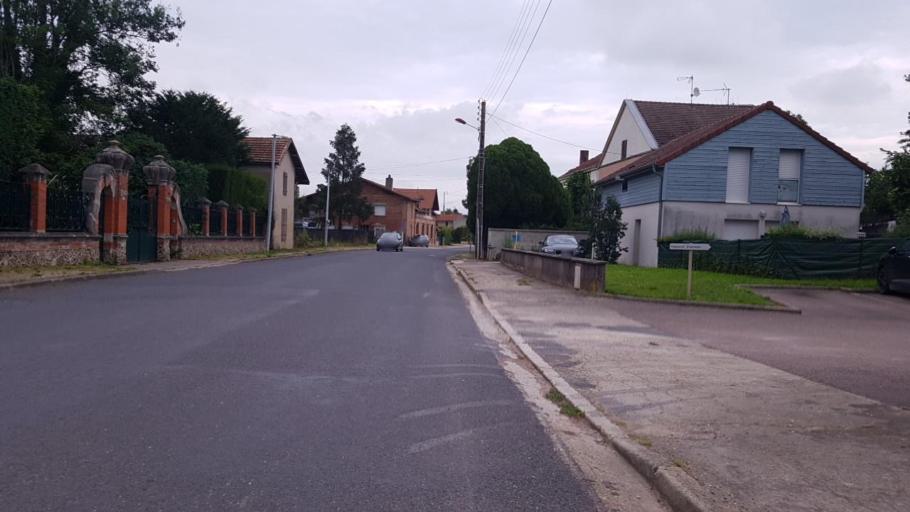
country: FR
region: Champagne-Ardenne
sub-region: Departement de la Marne
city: Pargny-sur-Saulx
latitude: 48.7664
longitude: 4.8388
